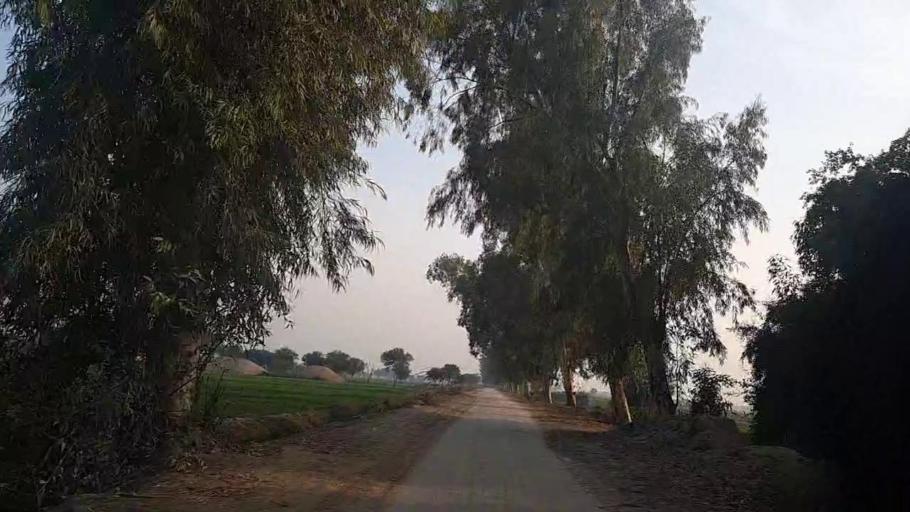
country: PK
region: Sindh
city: Sakrand
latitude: 26.1306
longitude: 68.2289
